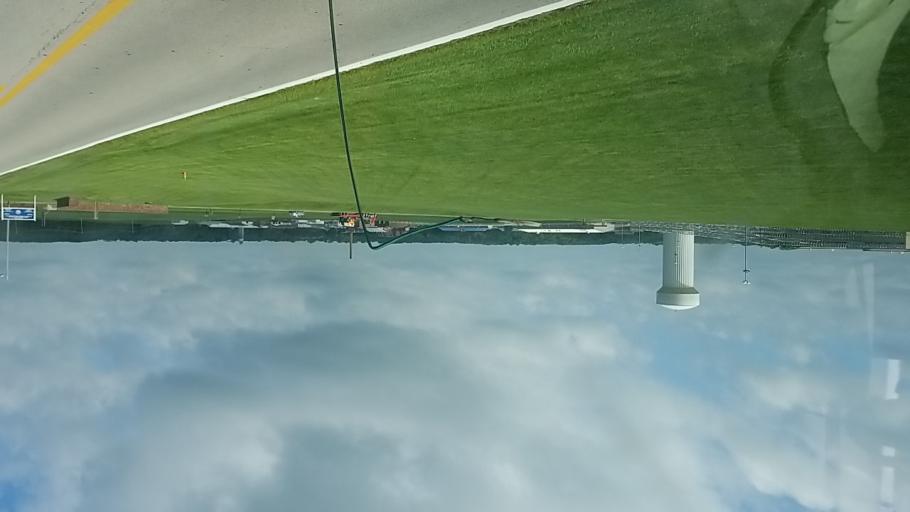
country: US
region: Ohio
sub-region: Franklin County
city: Grove City
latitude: 39.8029
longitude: -83.1501
